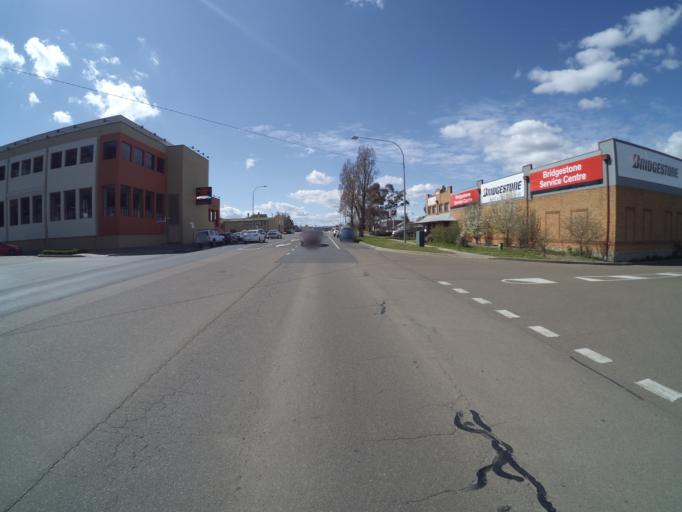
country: AU
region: New South Wales
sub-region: Goulburn Mulwaree
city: Goulburn
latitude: -34.7551
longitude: 149.7212
